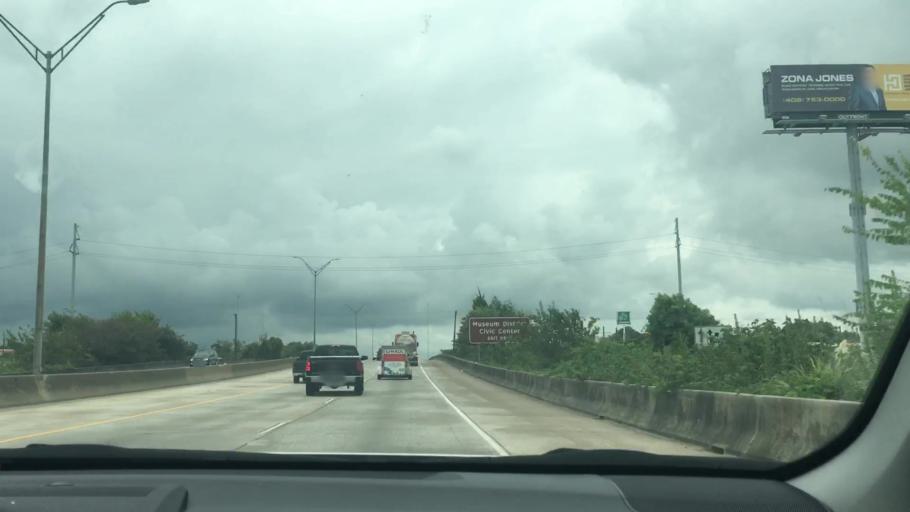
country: US
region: Texas
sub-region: Jefferson County
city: Beaumont
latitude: 30.0960
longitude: -94.1137
